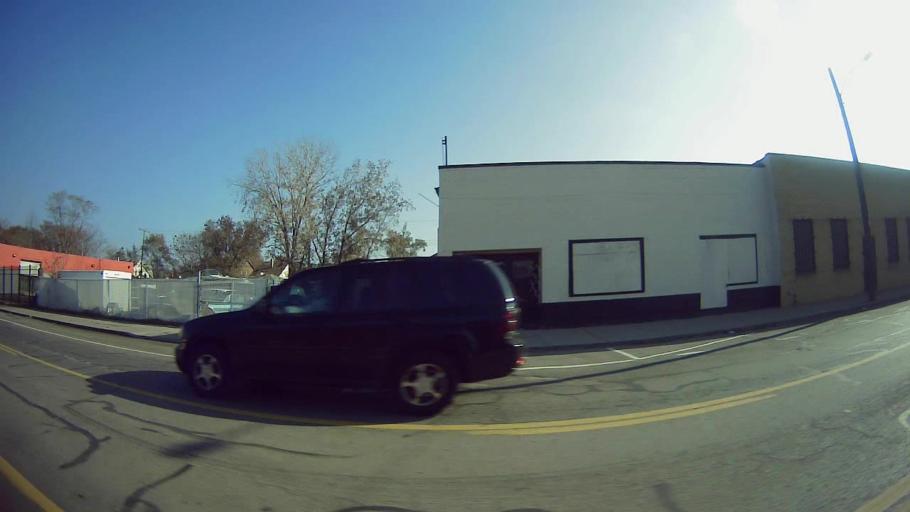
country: US
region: Michigan
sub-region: Wayne County
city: Dearborn
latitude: 42.3713
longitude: -83.1780
